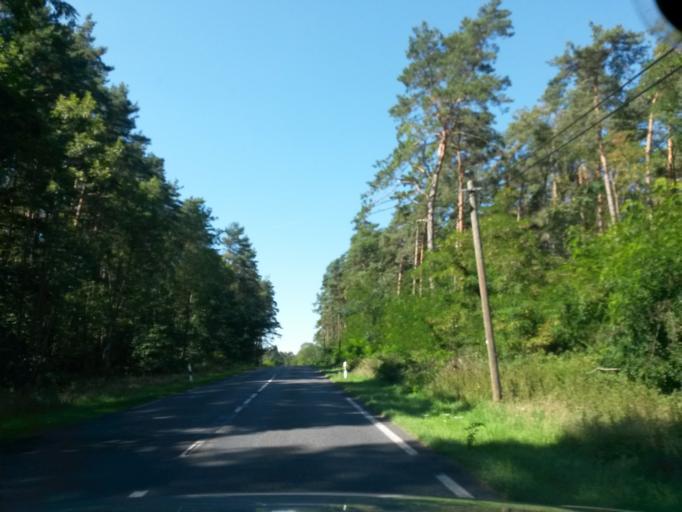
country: DE
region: Brandenburg
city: Lychen
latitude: 53.2205
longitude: 13.3333
